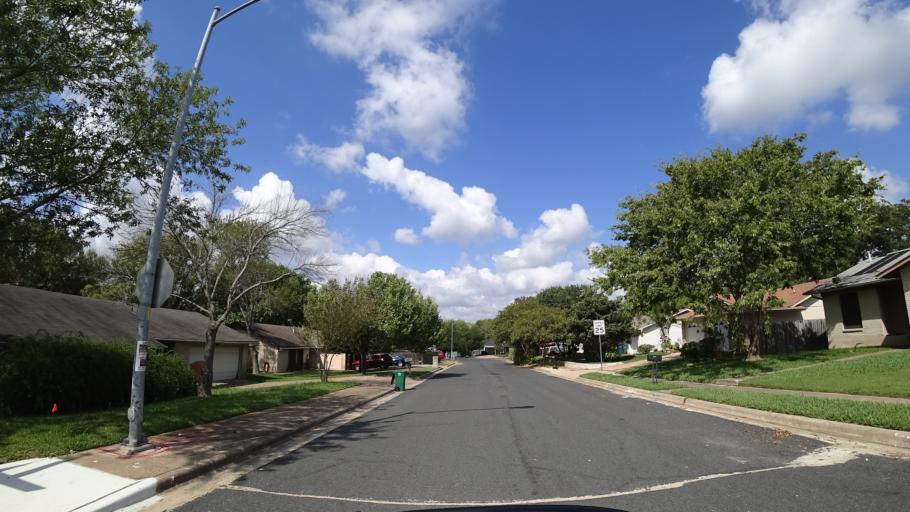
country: US
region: Texas
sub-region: Travis County
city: Onion Creek
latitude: 30.1971
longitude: -97.7964
